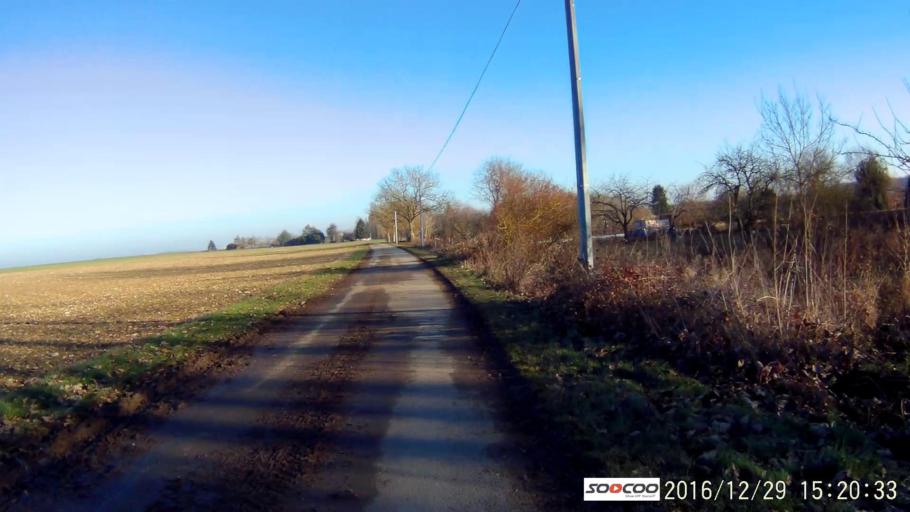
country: FR
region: Centre
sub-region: Departement de l'Indre
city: Neuvy-Pailloux
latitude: 46.9373
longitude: 1.8081
